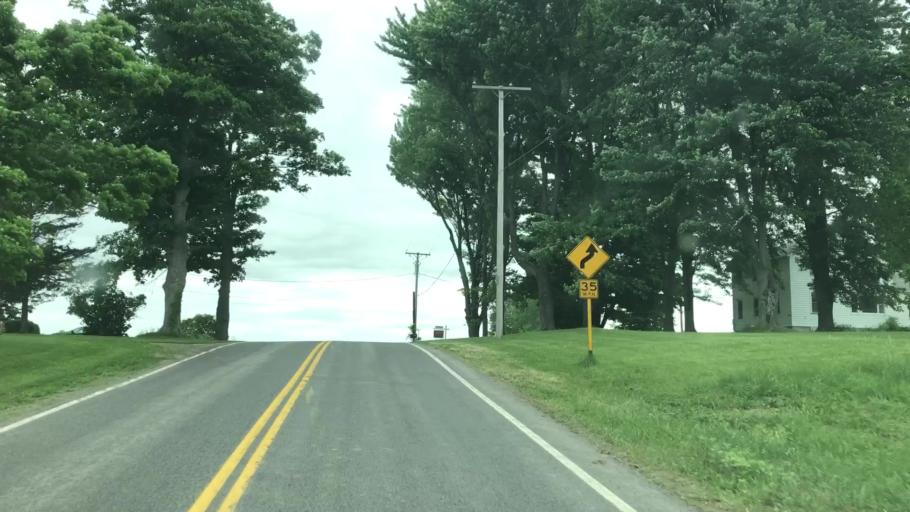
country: US
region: New York
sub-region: Wayne County
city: Macedon
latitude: 43.1163
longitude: -77.2840
